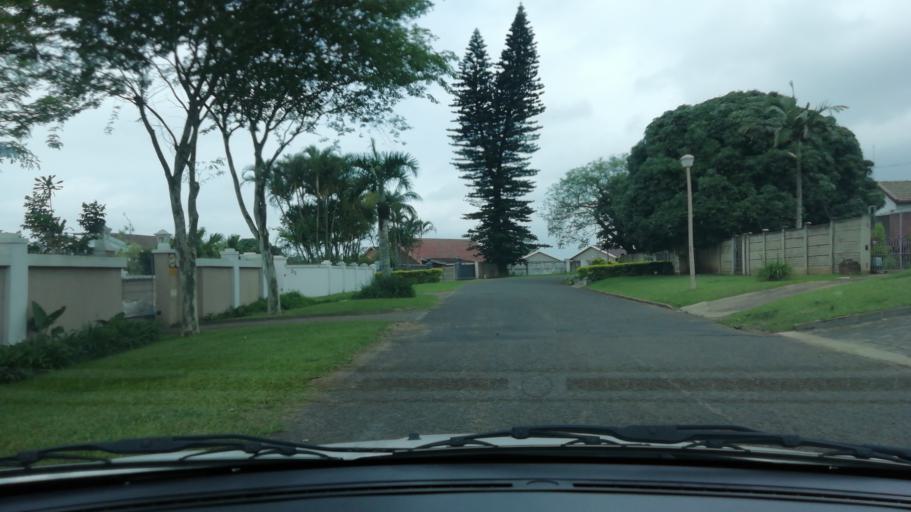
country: ZA
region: KwaZulu-Natal
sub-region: uThungulu District Municipality
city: Empangeni
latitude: -28.7356
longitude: 31.9005
